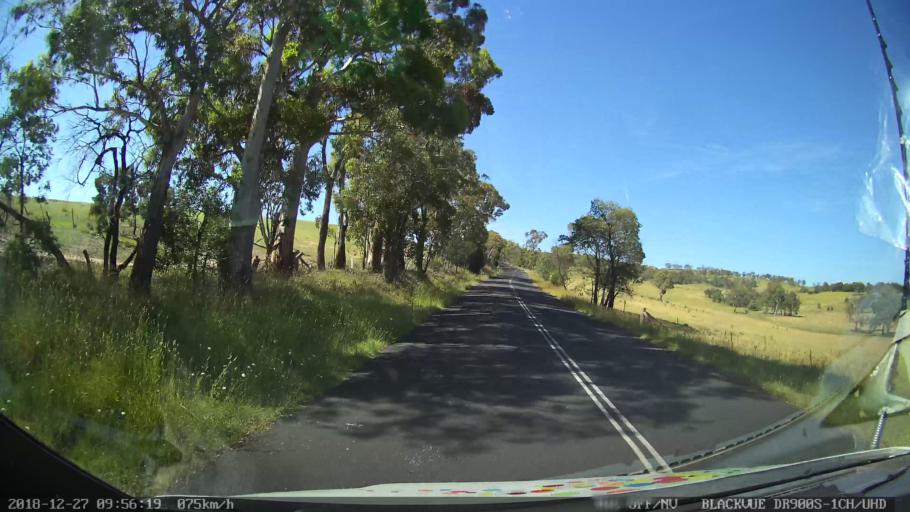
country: AU
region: New South Wales
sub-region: Lithgow
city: Portland
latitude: -33.4111
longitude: 149.9723
